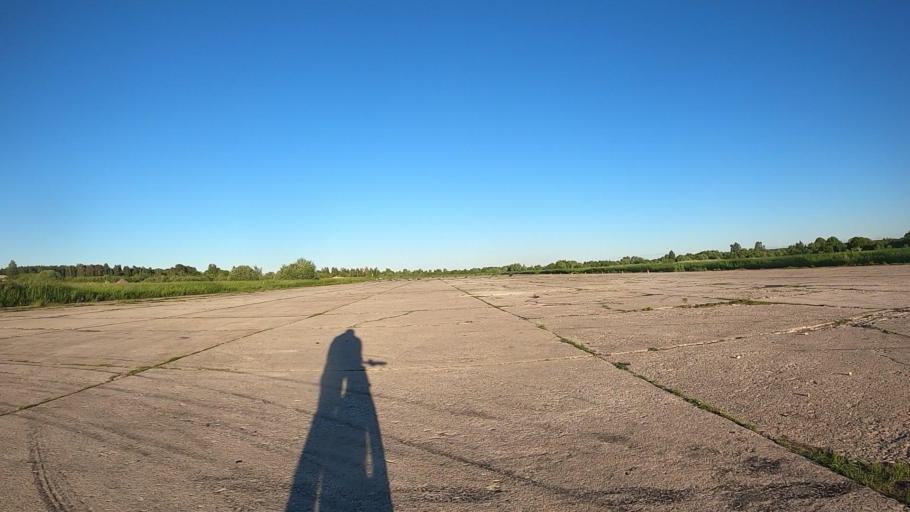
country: LV
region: Kekava
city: Kekava
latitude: 56.8822
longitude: 24.2291
